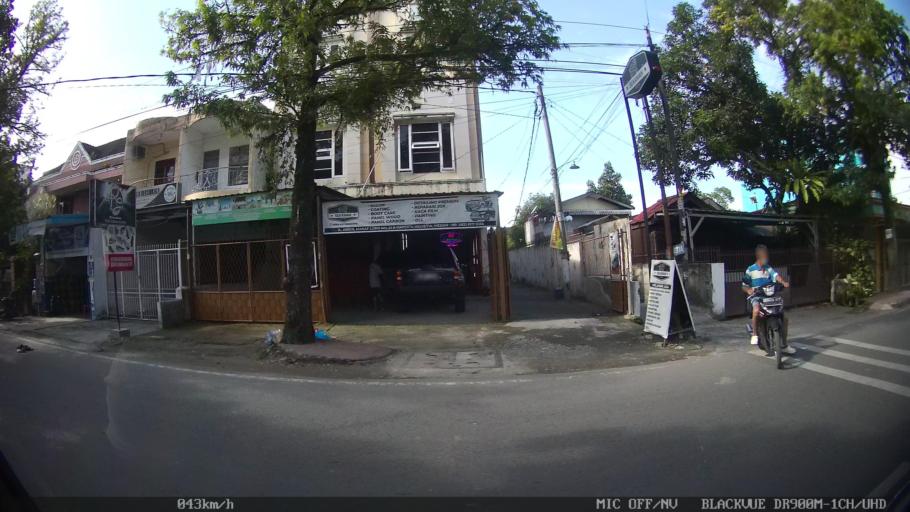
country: ID
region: North Sumatra
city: Medan
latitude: 3.6047
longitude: 98.6469
